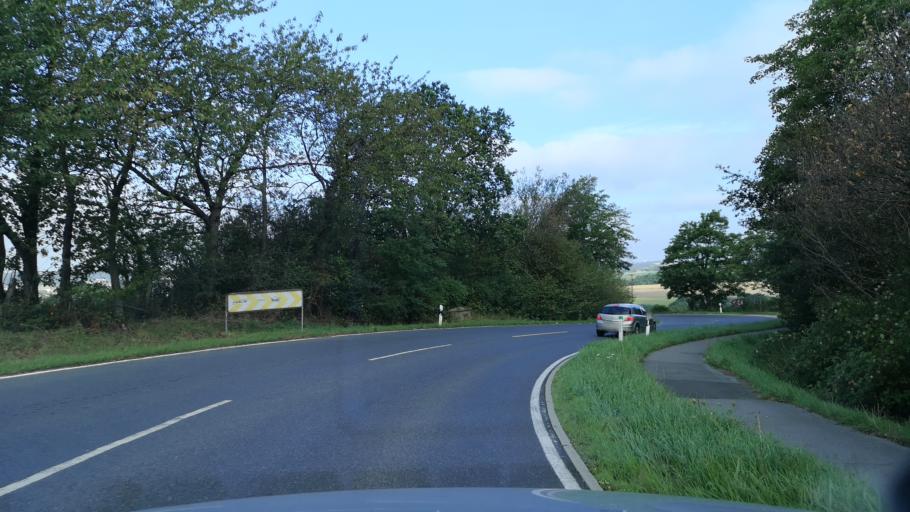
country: DE
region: North Rhine-Westphalia
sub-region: Regierungsbezirk Dusseldorf
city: Wuppertal
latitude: 51.3061
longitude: 7.1346
